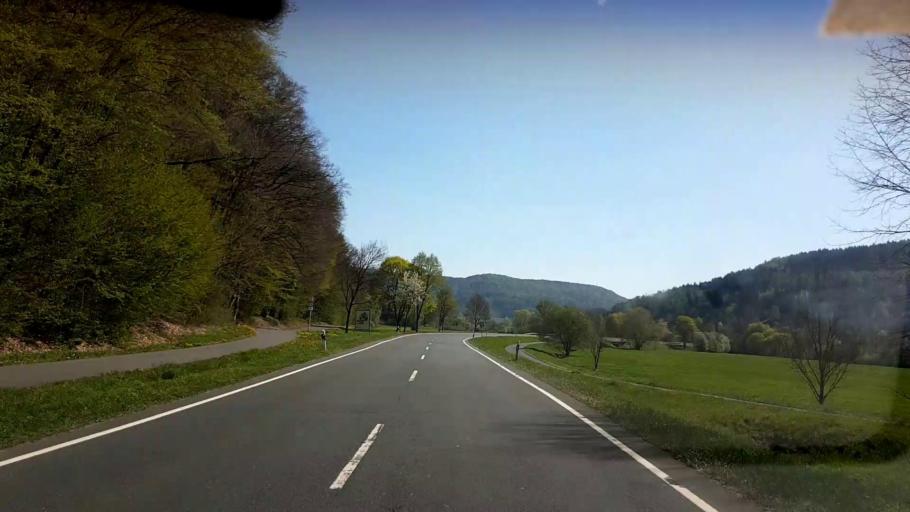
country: DE
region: Bavaria
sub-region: Upper Franconia
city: Unterleinleiter
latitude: 49.8087
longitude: 11.1951
